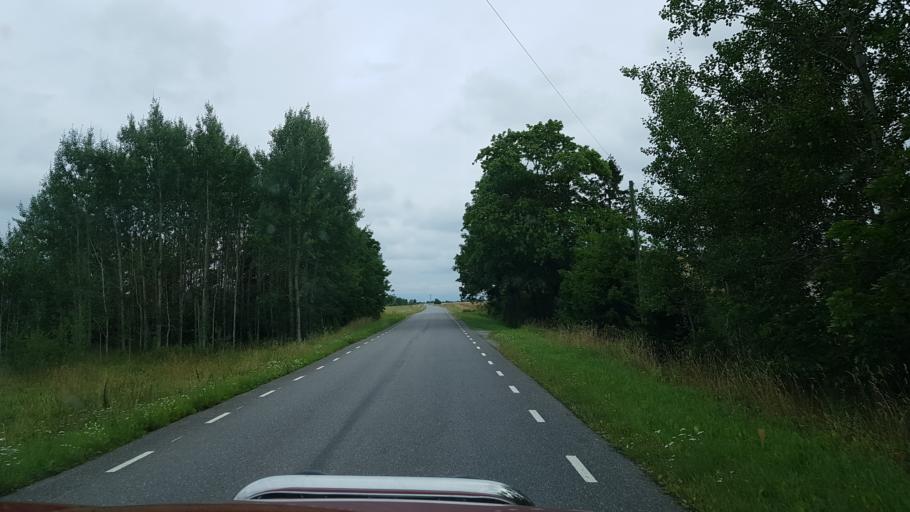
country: EE
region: Ida-Virumaa
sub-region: Kivioli linn
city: Kivioli
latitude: 59.4091
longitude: 27.0046
